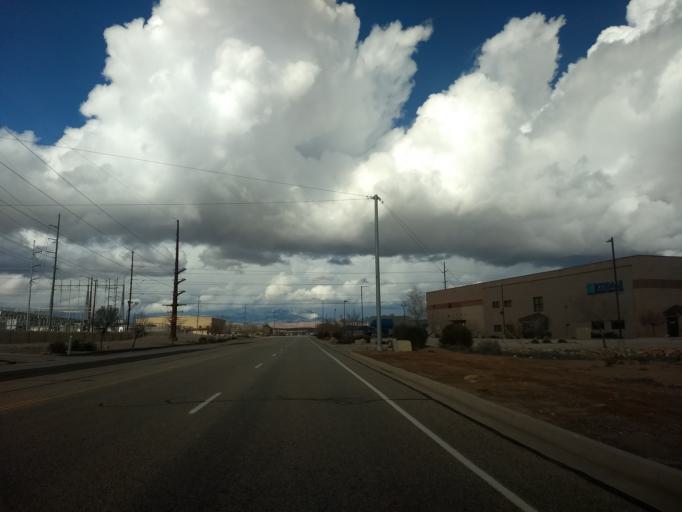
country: US
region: Utah
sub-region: Washington County
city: Saint George
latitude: 37.0294
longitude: -113.5626
